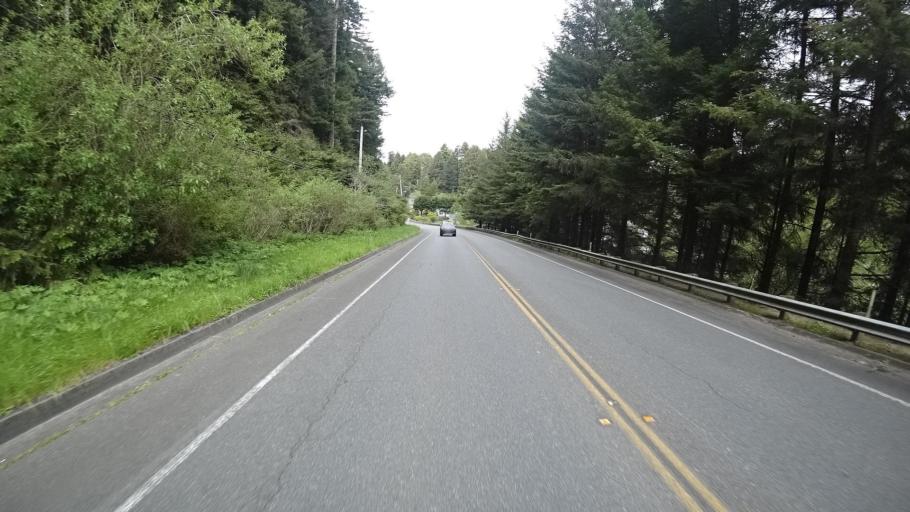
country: US
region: California
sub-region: Humboldt County
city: Cutten
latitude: 40.7670
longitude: -124.1556
